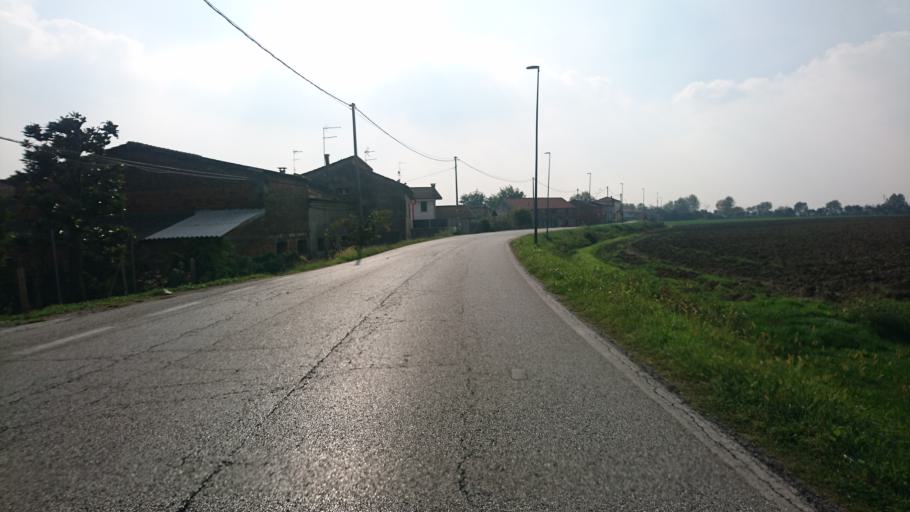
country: IT
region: Veneto
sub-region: Provincia di Rovigo
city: Grignano Polesine
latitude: 45.0298
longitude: 11.7494
